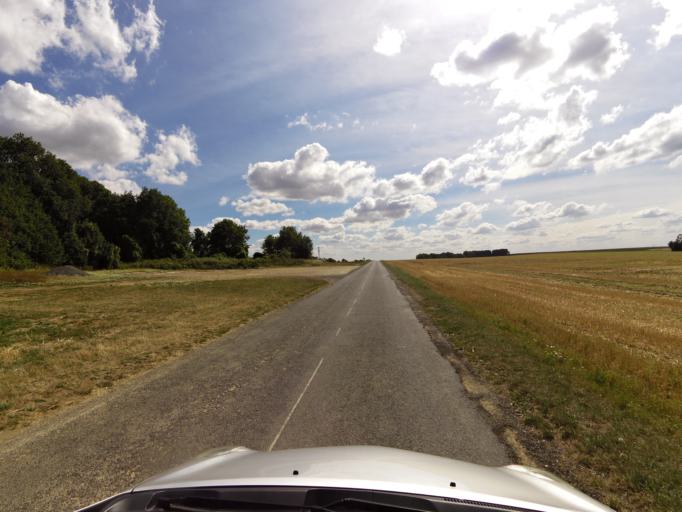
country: FR
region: Picardie
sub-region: Departement de l'Aisne
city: Bruyeres-et-Montberault
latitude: 49.5005
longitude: 3.6269
